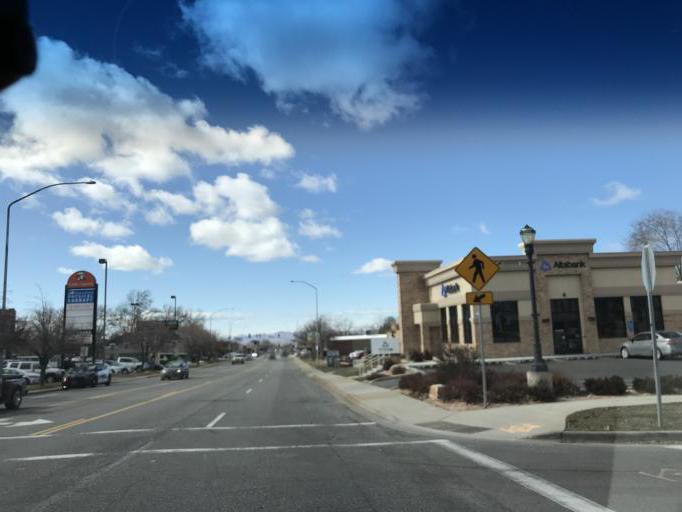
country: US
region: Utah
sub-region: Davis County
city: Bountiful
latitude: 40.8844
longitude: -111.8784
